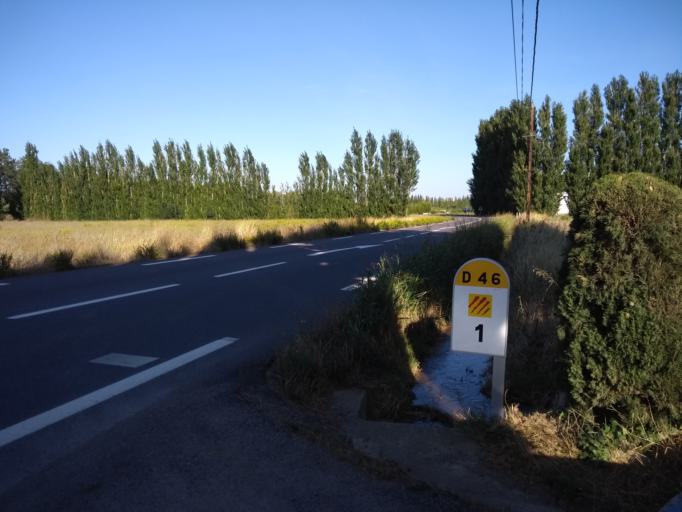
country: FR
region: Languedoc-Roussillon
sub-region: Departement des Pyrenees-Orientales
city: Millas
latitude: 42.6833
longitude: 2.6912
